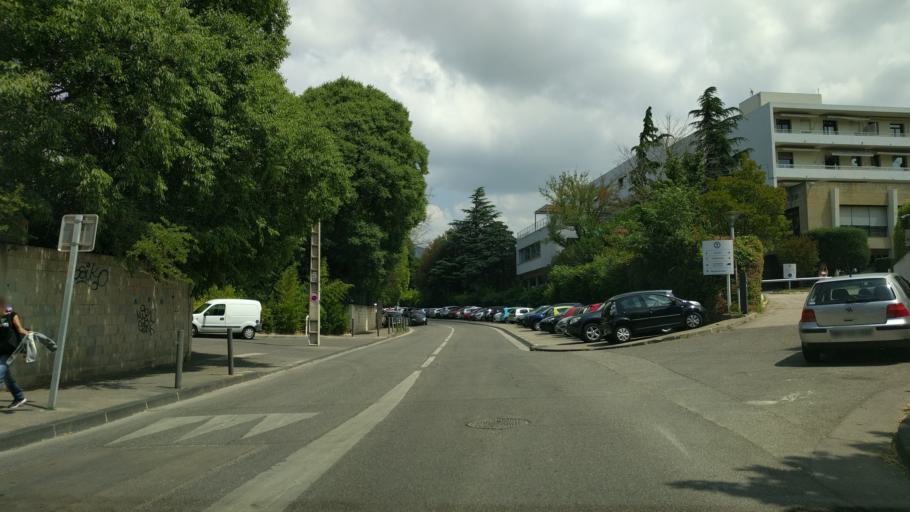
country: FR
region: Provence-Alpes-Cote d'Azur
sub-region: Departement des Bouches-du-Rhone
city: La Penne-sur-Huveaune
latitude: 43.3014
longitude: 5.5043
